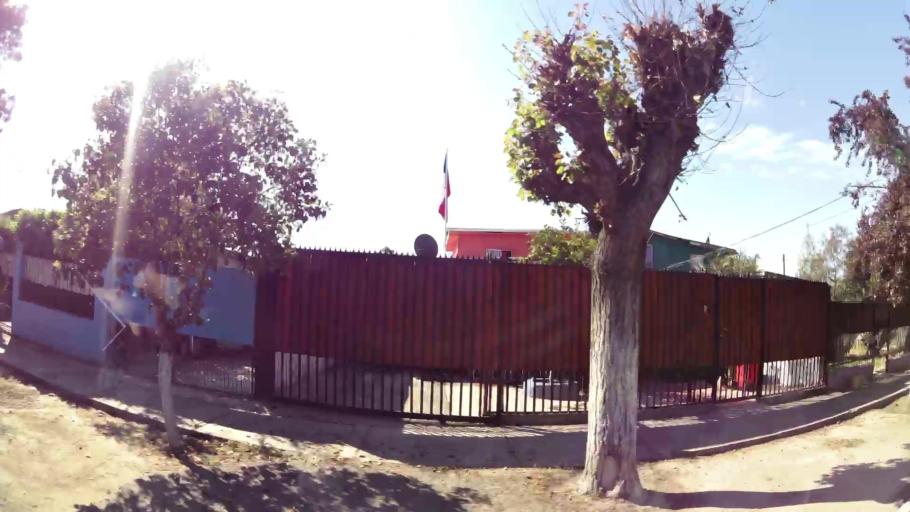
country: CL
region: Santiago Metropolitan
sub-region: Provincia de Santiago
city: La Pintana
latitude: -33.5346
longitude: -70.6171
